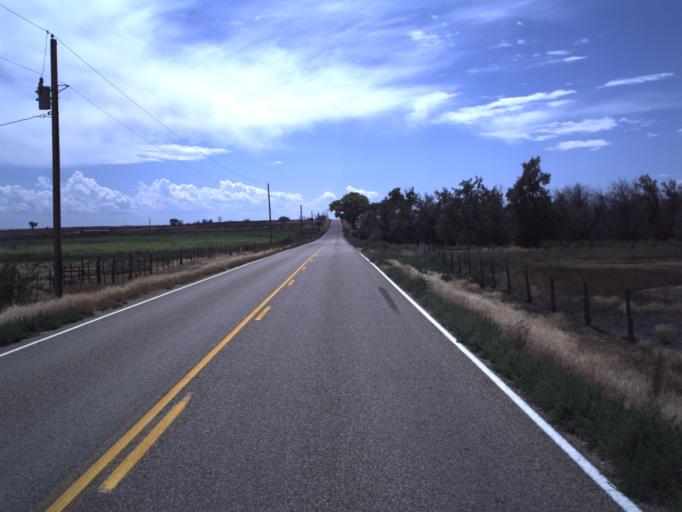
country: US
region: Utah
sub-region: Uintah County
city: Maeser
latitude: 40.2445
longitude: -109.6844
